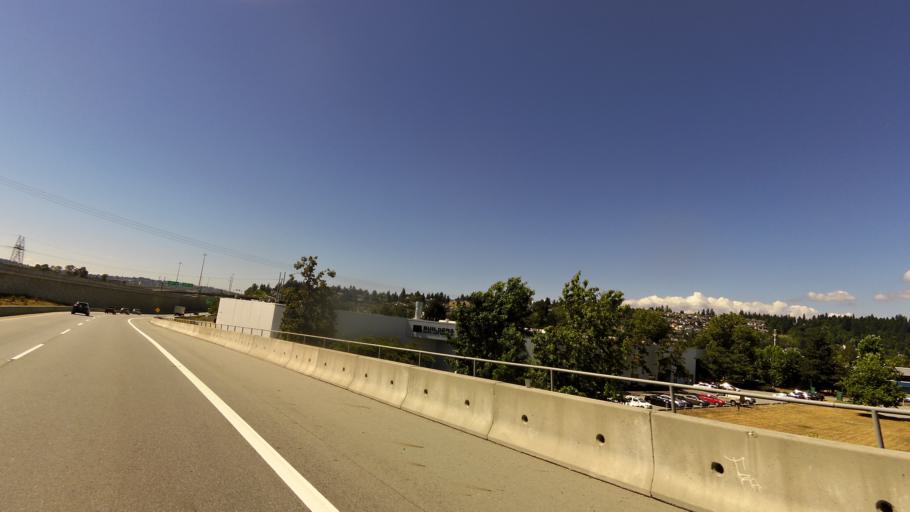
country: CA
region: British Columbia
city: Port Moody
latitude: 49.2284
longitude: -122.8216
